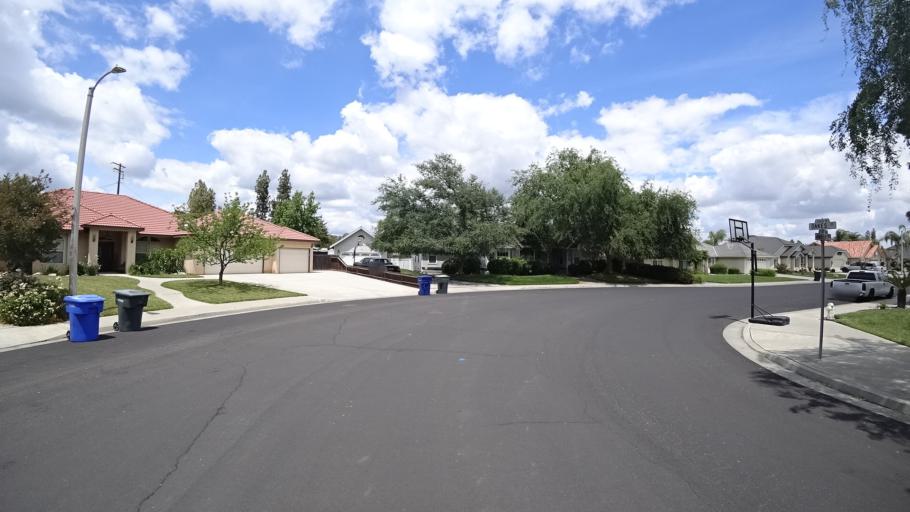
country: US
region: California
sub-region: Kings County
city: Hanford
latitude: 36.3530
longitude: -119.6539
